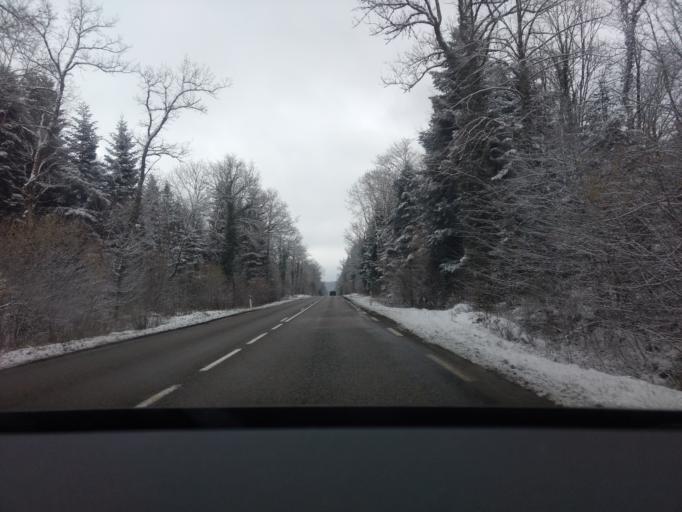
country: FR
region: Franche-Comte
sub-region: Departement du Jura
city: Arbois
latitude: 46.8086
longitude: 5.8087
